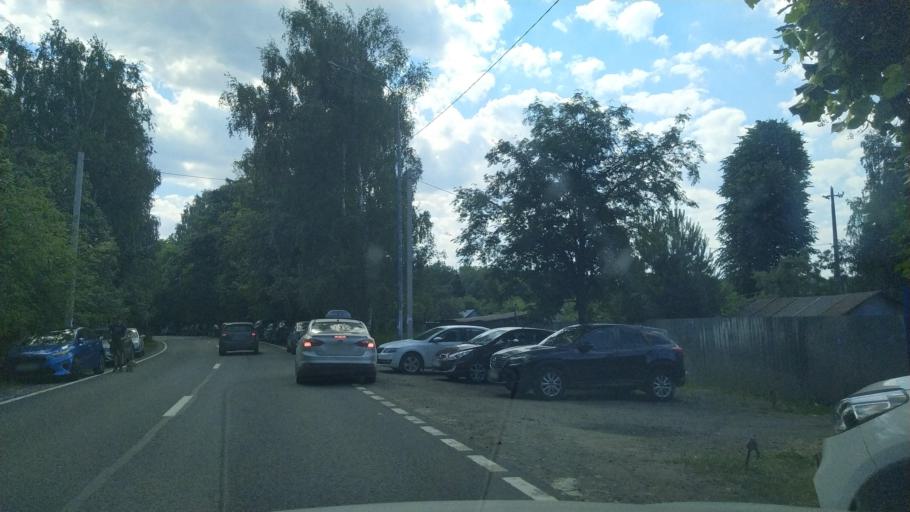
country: RU
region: St.-Petersburg
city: Kronshtadt
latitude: 60.0247
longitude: 29.6835
